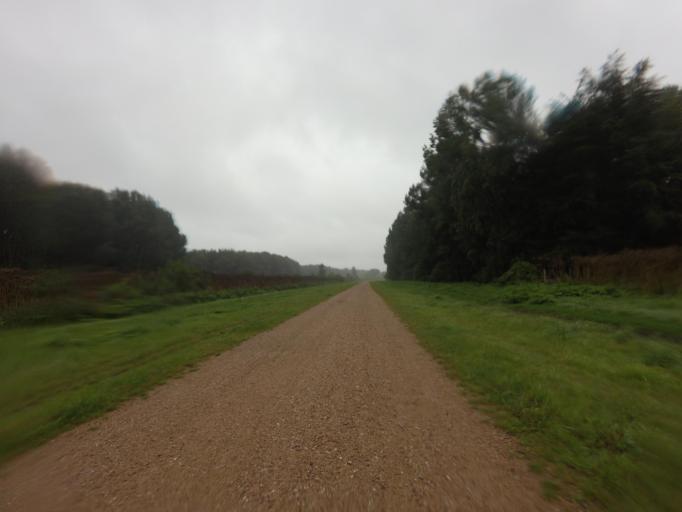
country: NL
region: North Holland
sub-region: Gemeente Huizen
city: Huizen
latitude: 52.3390
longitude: 5.2566
